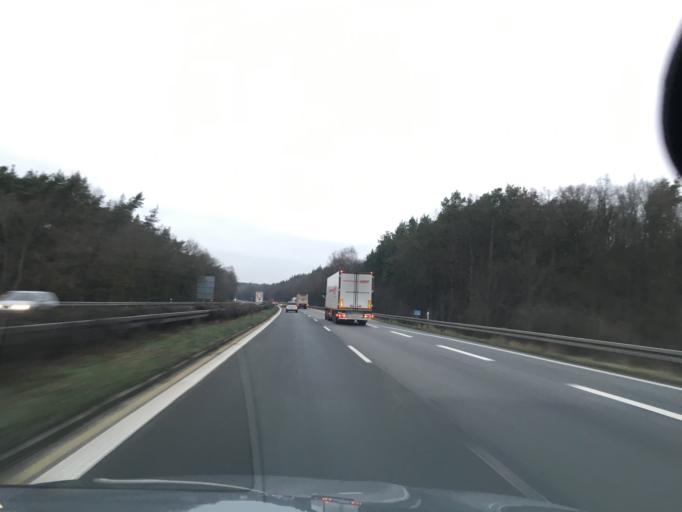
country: DE
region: Bavaria
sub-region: Regierungsbezirk Mittelfranken
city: Hochstadt an der Aisch
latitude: 49.7295
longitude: 10.8186
